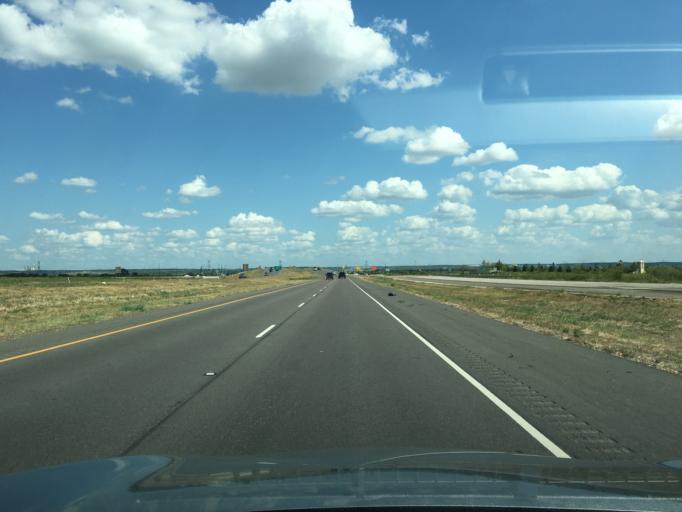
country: US
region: Texas
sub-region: Tarrant County
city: Mansfield
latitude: 32.5255
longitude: -97.0886
